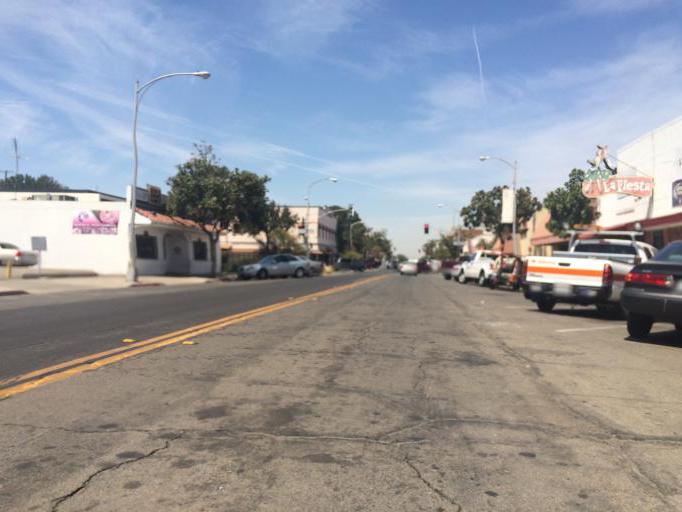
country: US
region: California
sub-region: Fresno County
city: Fresno
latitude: 36.7290
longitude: -119.7933
